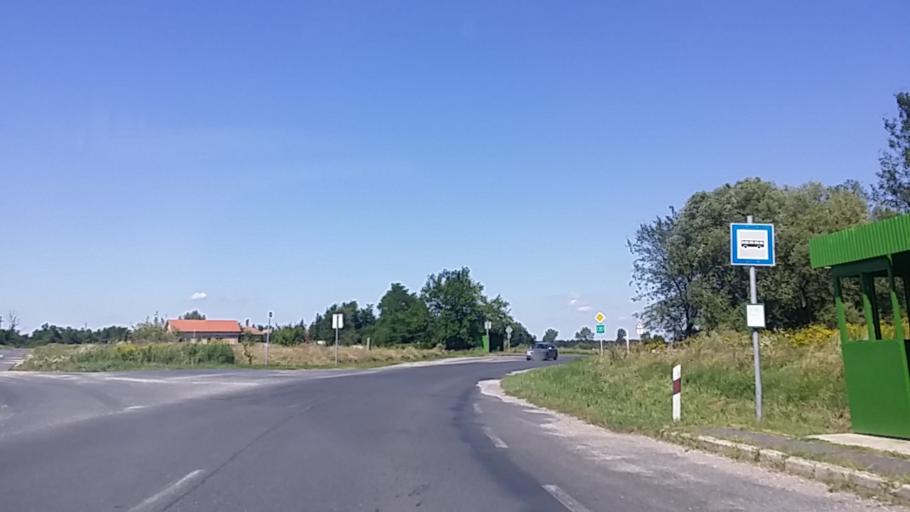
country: HU
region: Veszprem
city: Tapolca
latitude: 46.8693
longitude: 17.3851
